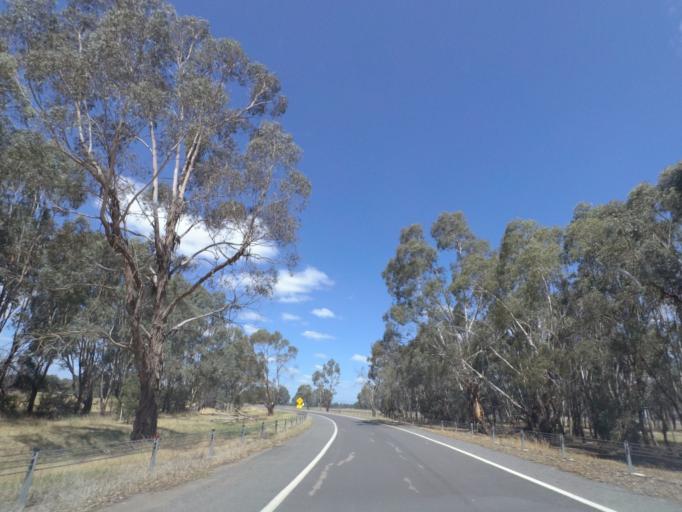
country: AU
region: Victoria
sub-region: Wangaratta
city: Wangaratta
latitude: -36.4029
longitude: 146.2995
